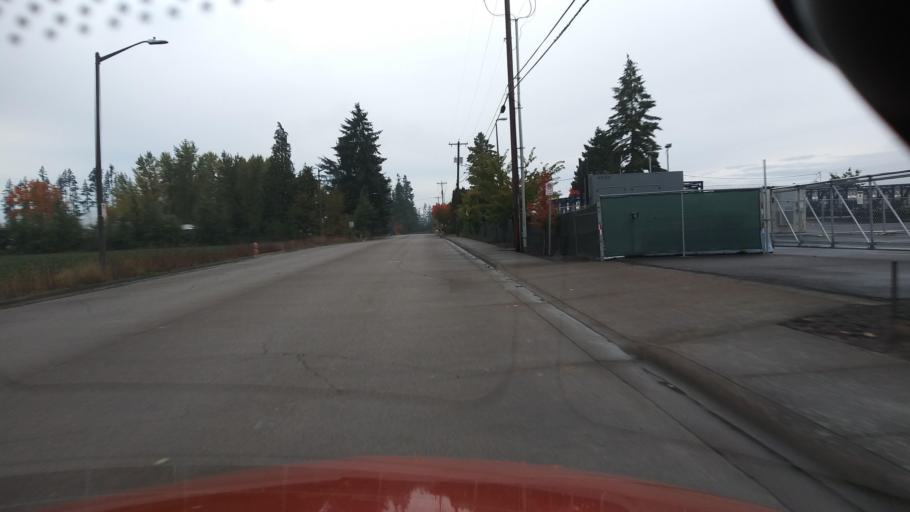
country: US
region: Oregon
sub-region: Washington County
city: Cornelius
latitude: 45.5250
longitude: -123.0666
